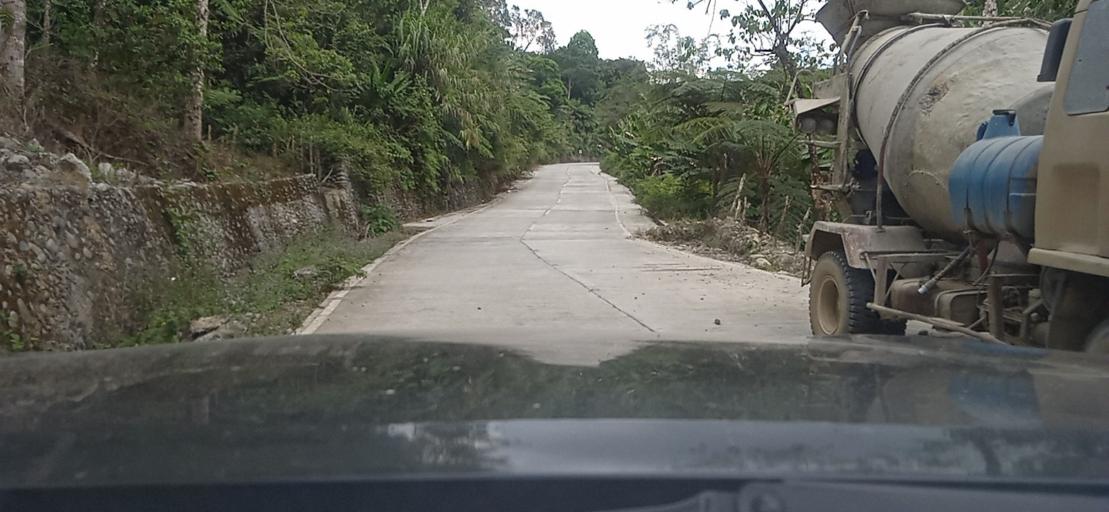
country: PH
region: Cordillera
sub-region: Kalinga
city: Lubuagan
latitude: 17.3744
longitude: 121.1809
